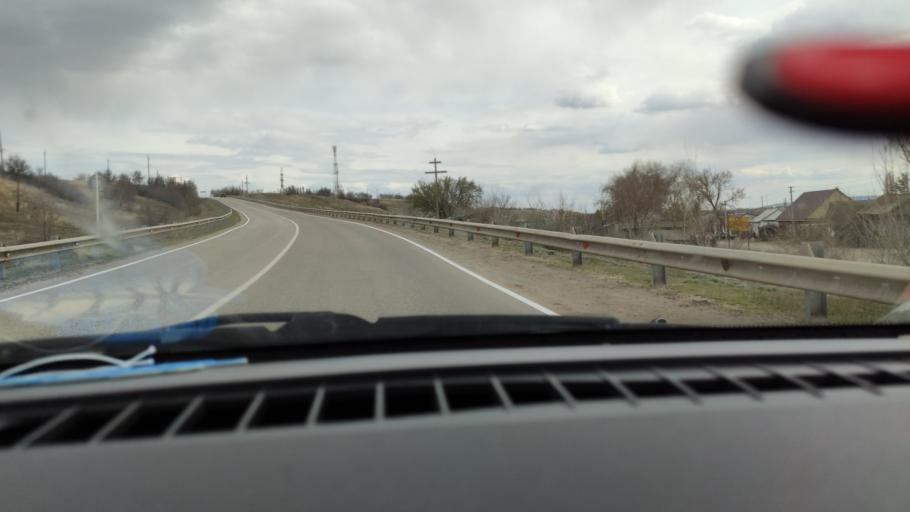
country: RU
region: Saratov
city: Privolzhskiy
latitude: 51.1788
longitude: 45.9242
